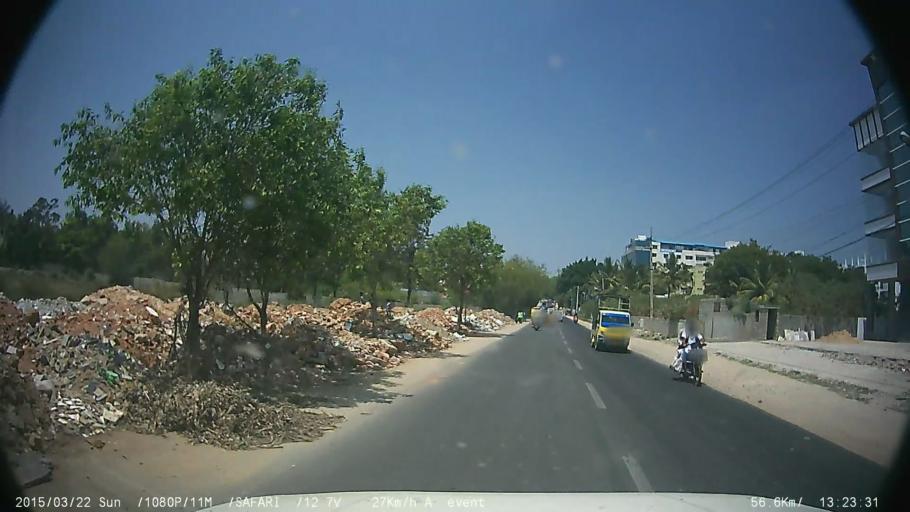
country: IN
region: Karnataka
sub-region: Bangalore Urban
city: Bangalore
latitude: 12.8625
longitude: 77.5906
